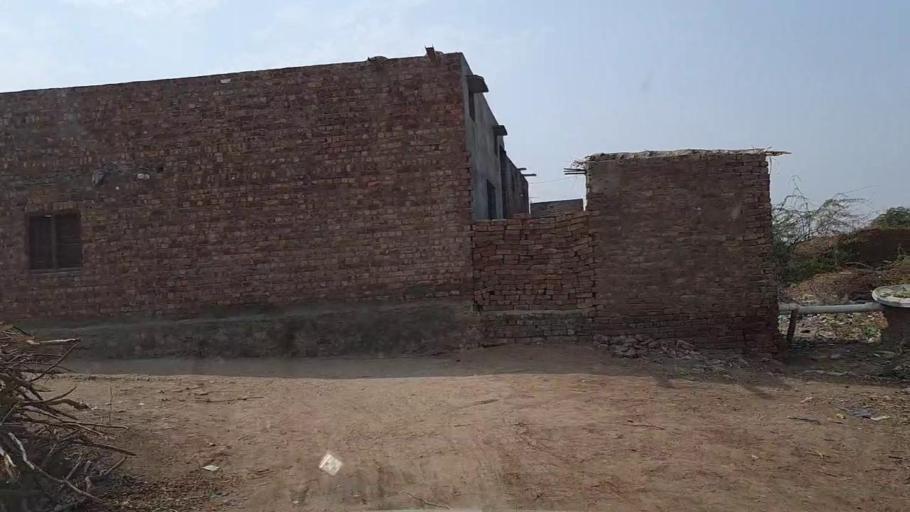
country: PK
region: Sindh
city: Mirwah Gorchani
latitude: 25.3286
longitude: 69.0319
